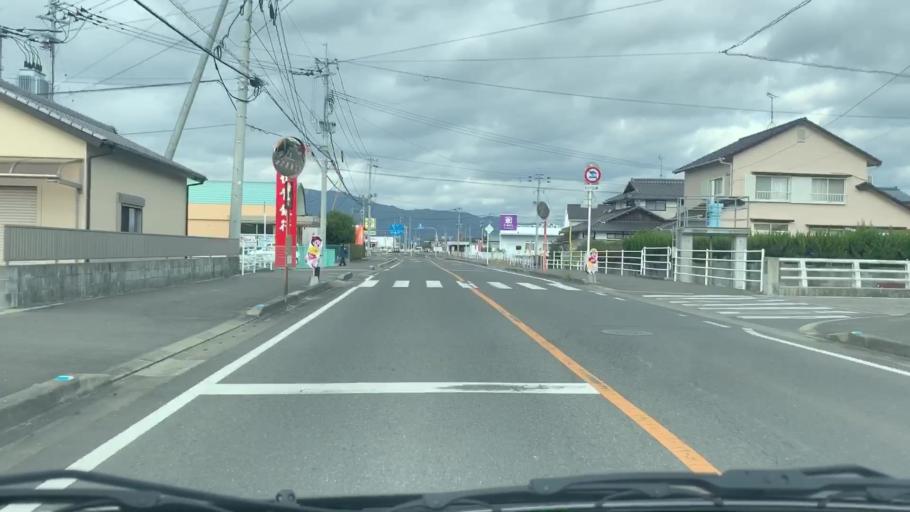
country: JP
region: Saga Prefecture
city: Saga-shi
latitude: 33.2471
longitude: 130.2377
